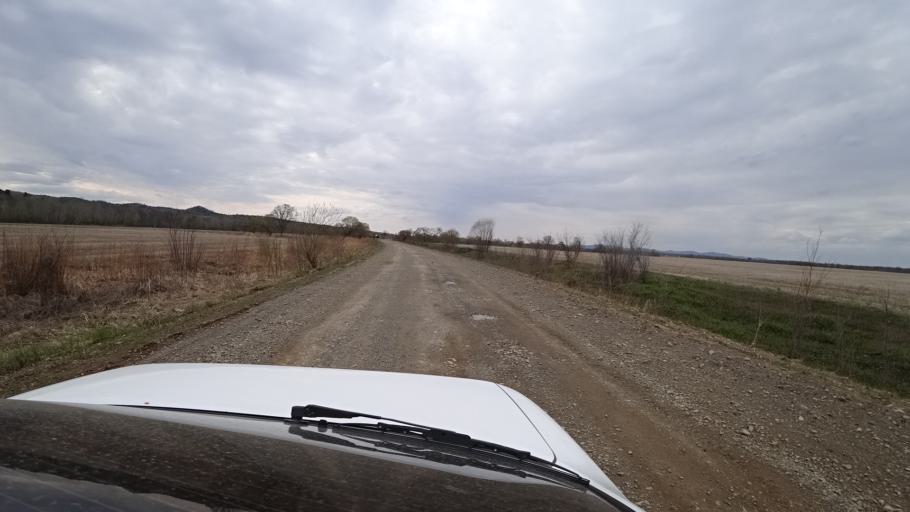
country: RU
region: Primorskiy
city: Novopokrovka
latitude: 45.4892
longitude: 134.4618
